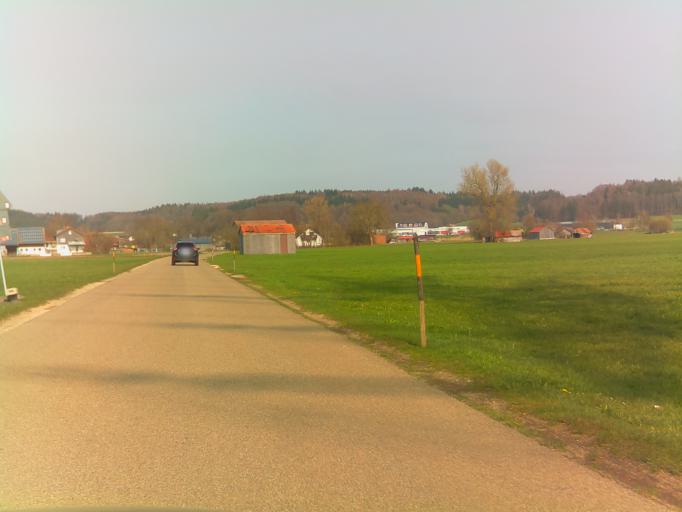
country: DE
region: Bavaria
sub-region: Swabia
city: Unterroth
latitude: 48.1893
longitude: 10.1624
